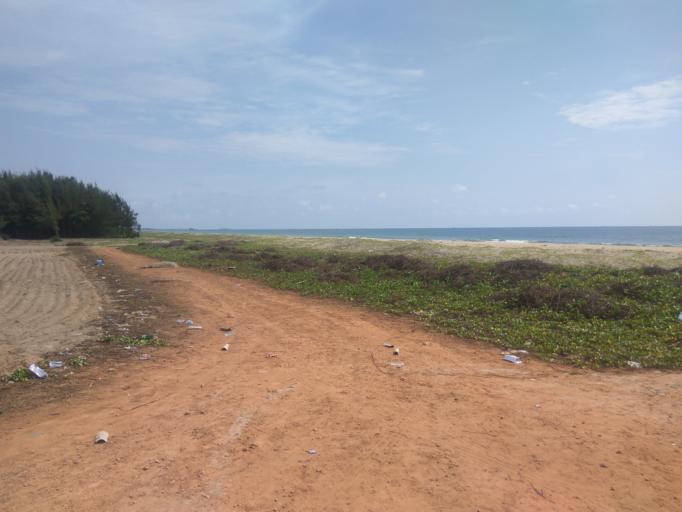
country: IN
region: Tamil Nadu
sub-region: Cuddalore
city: Alappakkam
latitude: 11.5676
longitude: 79.7576
